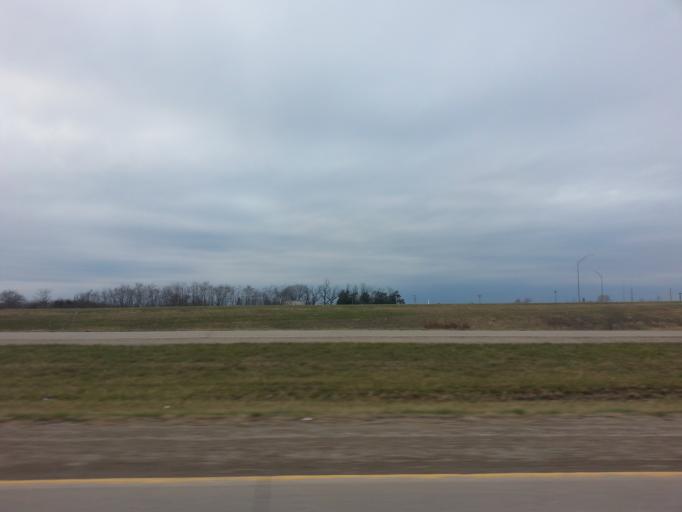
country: US
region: Iowa
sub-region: Henry County
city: Mount Pleasant
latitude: 40.9355
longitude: -91.5355
